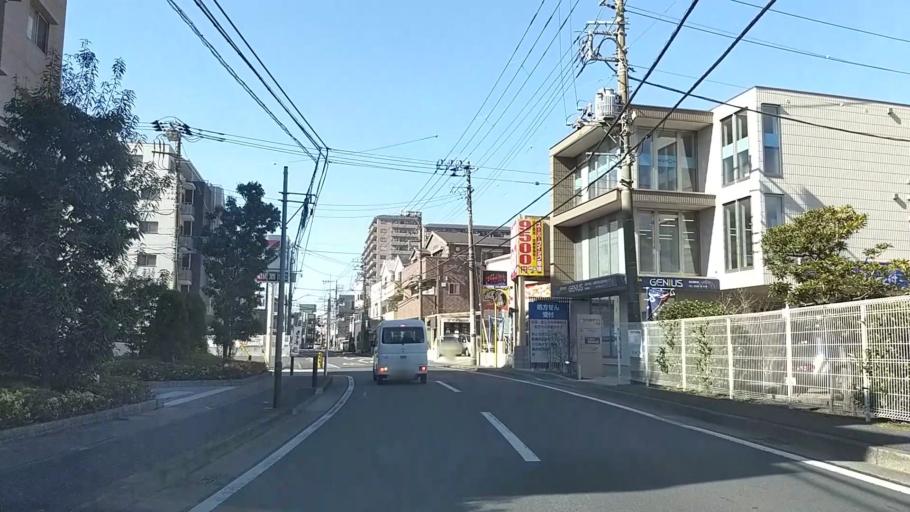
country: JP
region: Kanagawa
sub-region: Kawasaki-shi
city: Kawasaki
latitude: 35.5298
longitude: 139.6431
